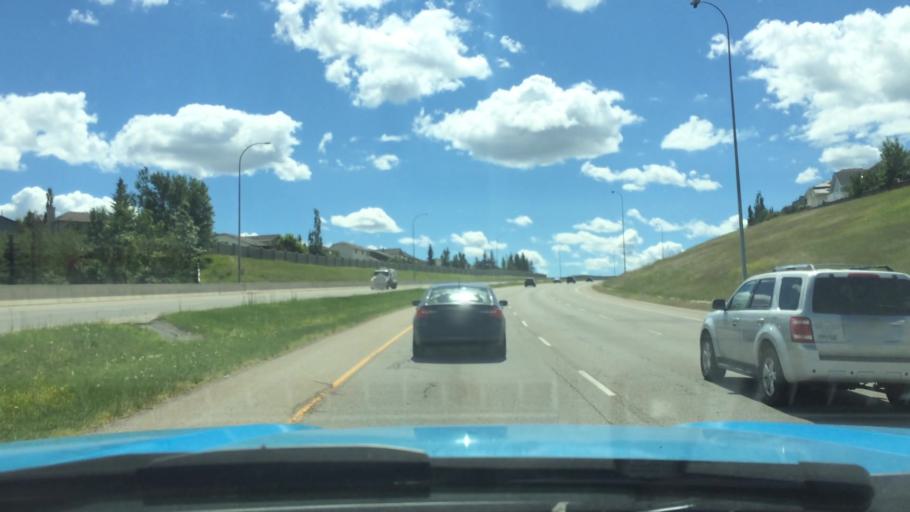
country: CA
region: Alberta
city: Calgary
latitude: 51.1357
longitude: -114.1217
